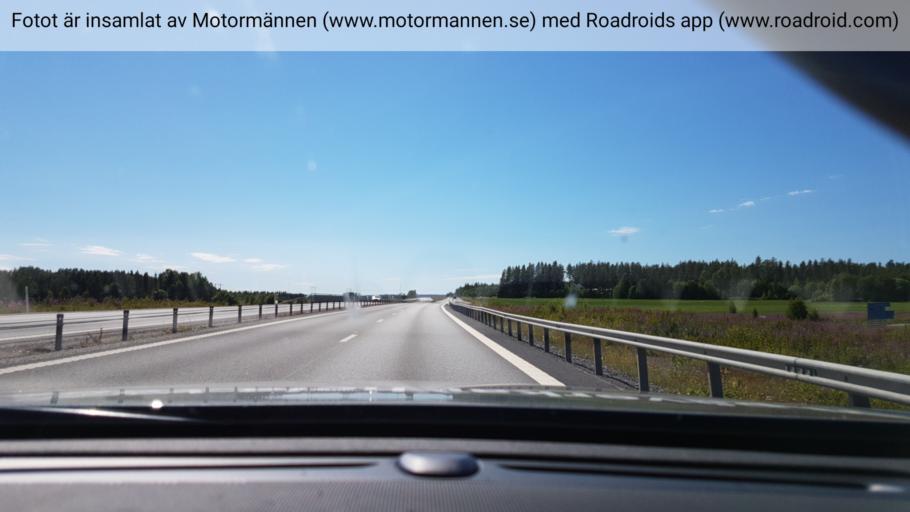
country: SE
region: Vaesterbotten
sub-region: Skelleftea Kommun
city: Kage
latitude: 64.8873
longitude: 21.0486
